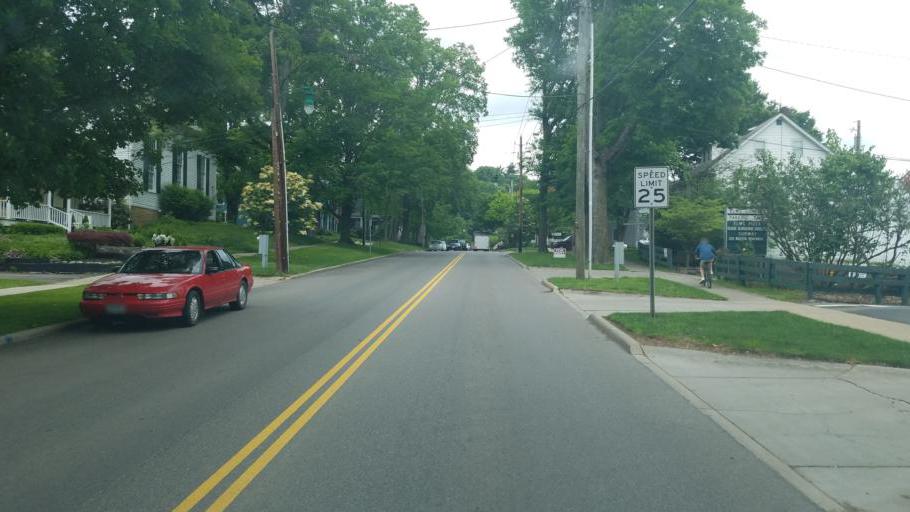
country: US
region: Ohio
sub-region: Licking County
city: Granville
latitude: 40.0662
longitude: -82.5202
